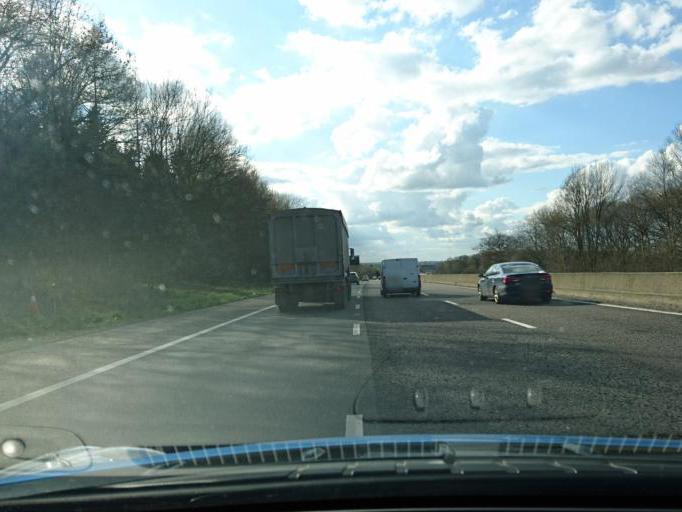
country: GB
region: England
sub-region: Borough of Swindon
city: Chiseldon
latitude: 51.5304
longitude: -1.7567
